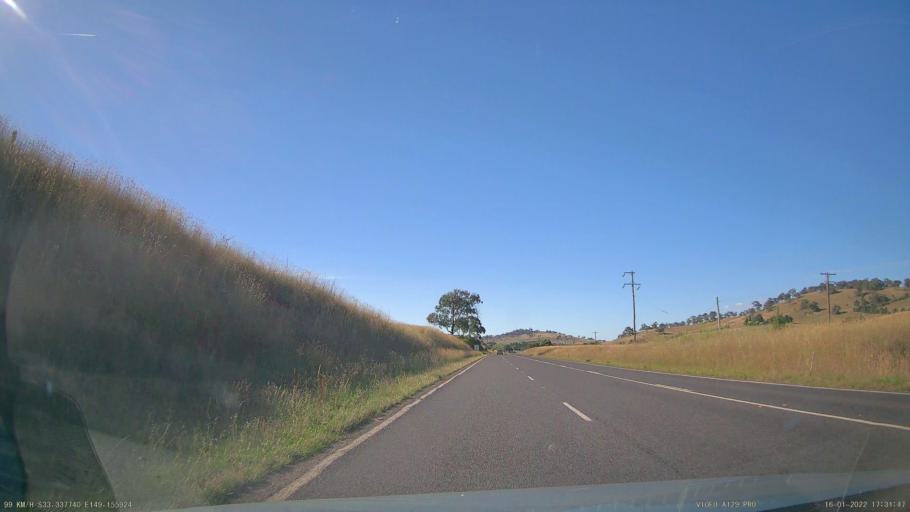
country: AU
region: New South Wales
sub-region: Orange Municipality
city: Orange
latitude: -33.3375
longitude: 149.1558
